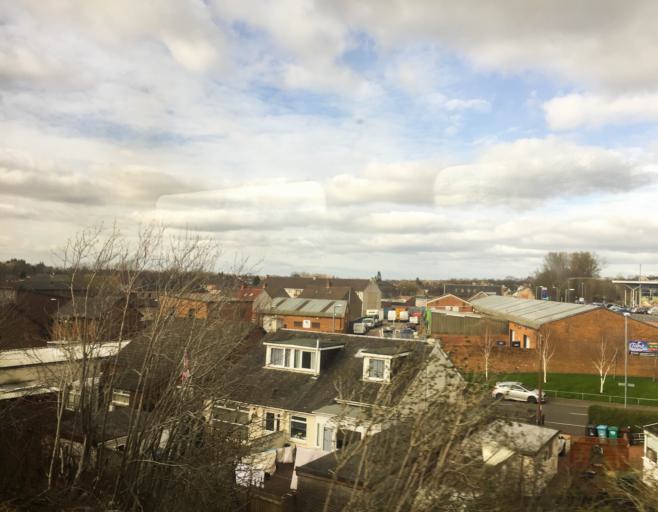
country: GB
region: Scotland
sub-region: North Lanarkshire
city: Wishaw
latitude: 55.7734
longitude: -3.9293
